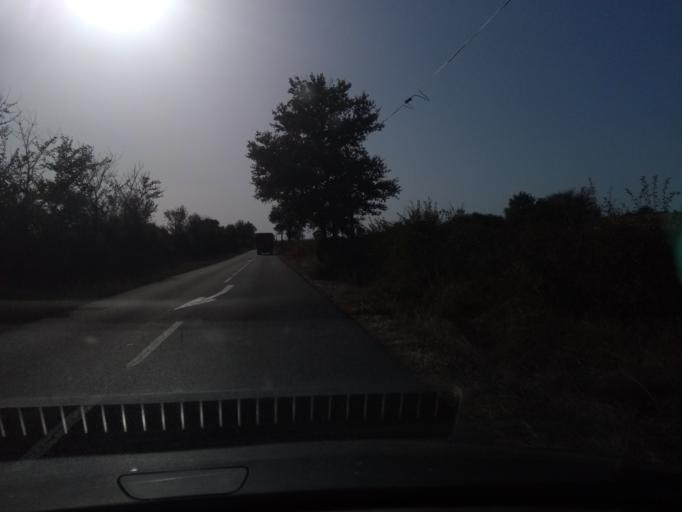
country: FR
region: Poitou-Charentes
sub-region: Departement de la Vienne
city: Lathus-Saint-Remy
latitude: 46.4503
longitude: 1.0024
